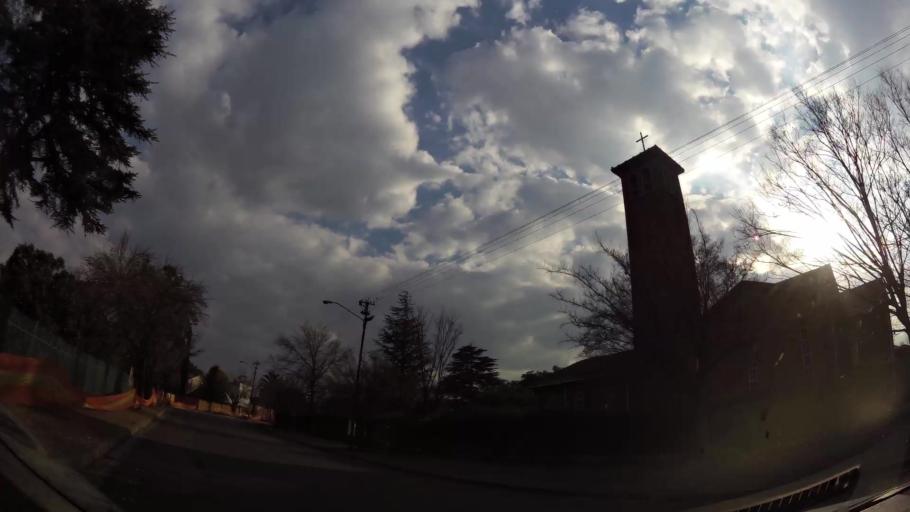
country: ZA
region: Gauteng
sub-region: Ekurhuleni Metropolitan Municipality
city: Germiston
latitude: -26.2422
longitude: 28.1797
